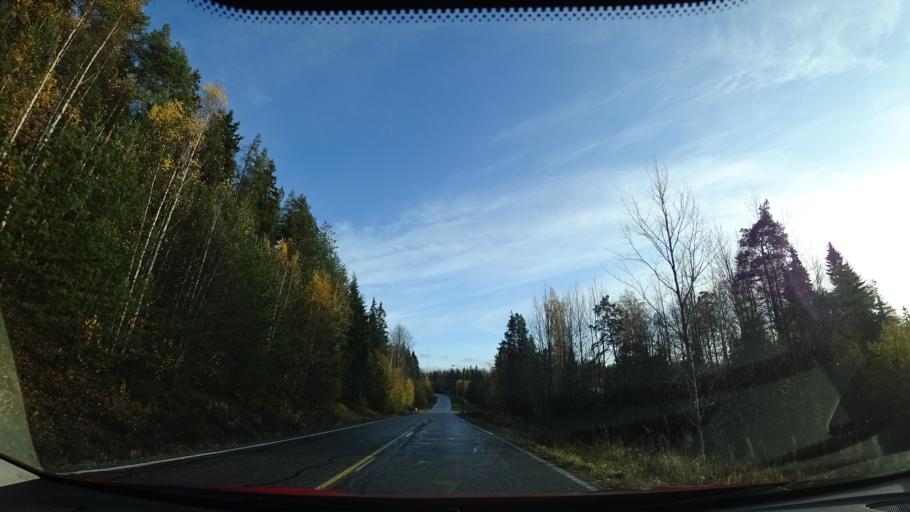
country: FI
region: Uusimaa
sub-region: Helsinki
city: Sibbo
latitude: 60.2719
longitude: 25.2018
